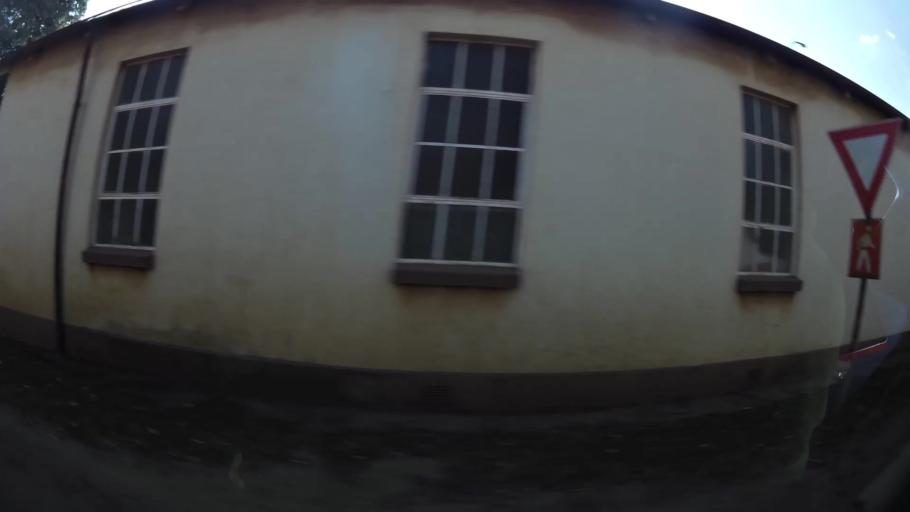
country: ZA
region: Gauteng
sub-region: Ekurhuleni Metropolitan Municipality
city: Benoni
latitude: -26.0972
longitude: 28.2961
